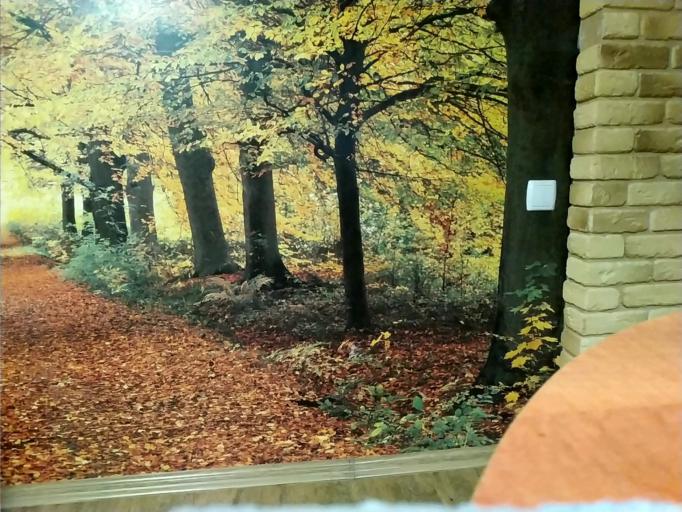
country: BY
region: Minsk
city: Plyeshchanitsy
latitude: 54.4265
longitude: 27.5846
